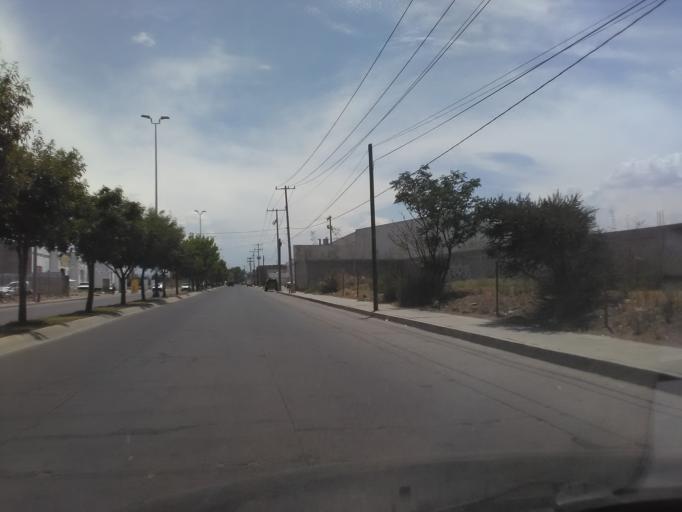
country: MX
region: Durango
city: Victoria de Durango
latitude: 24.0233
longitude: -104.6224
